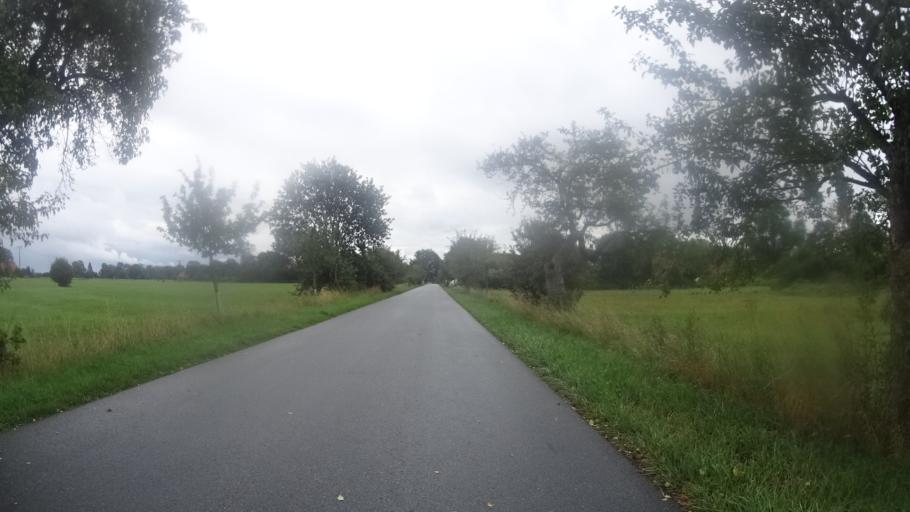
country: DE
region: Lower Saxony
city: Neu Darchau
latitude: 53.2420
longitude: 10.8913
